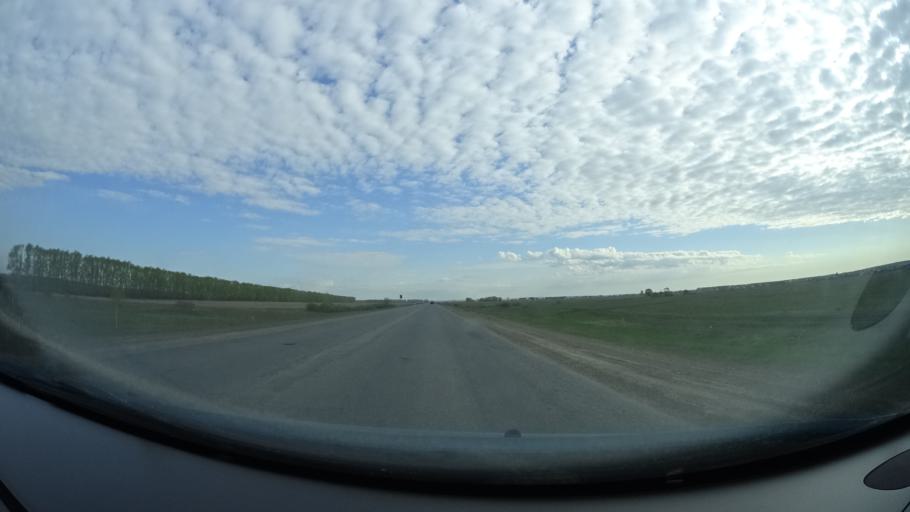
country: RU
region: Bashkortostan
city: Mikhaylovka
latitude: 54.9290
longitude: 55.7410
